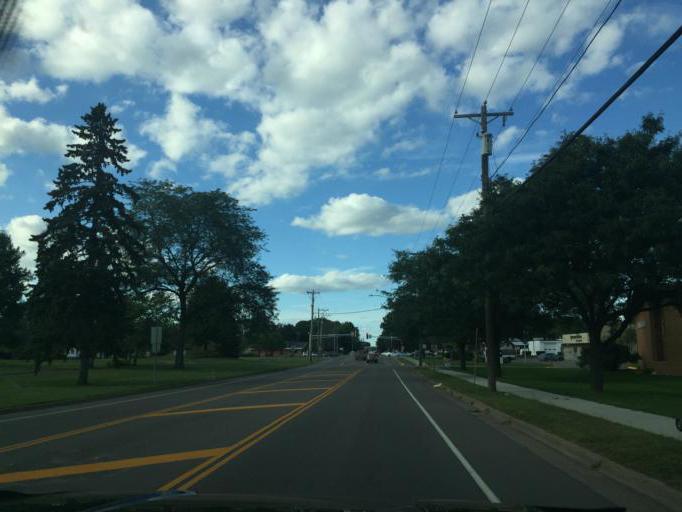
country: US
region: Minnesota
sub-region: Ramsey County
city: Roseville
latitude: 45.0048
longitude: -93.1463
